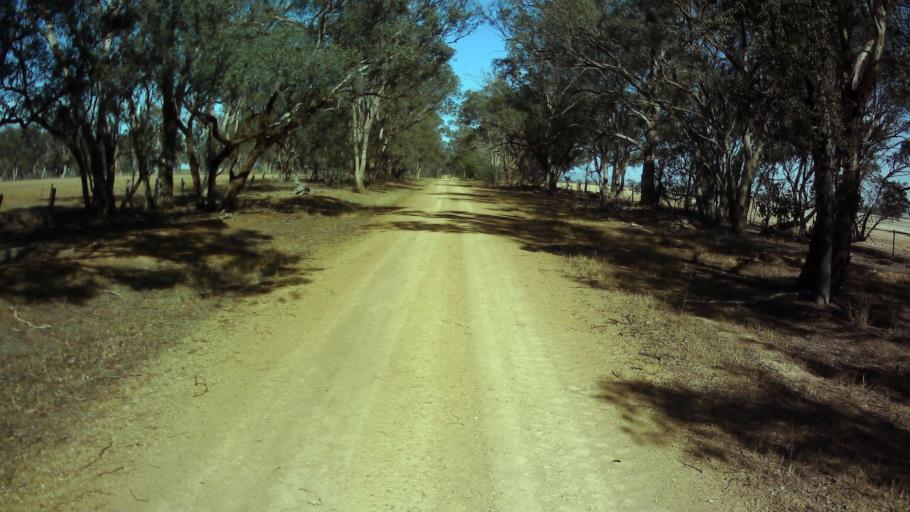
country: AU
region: New South Wales
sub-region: Weddin
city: Grenfell
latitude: -34.0487
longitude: 148.2893
